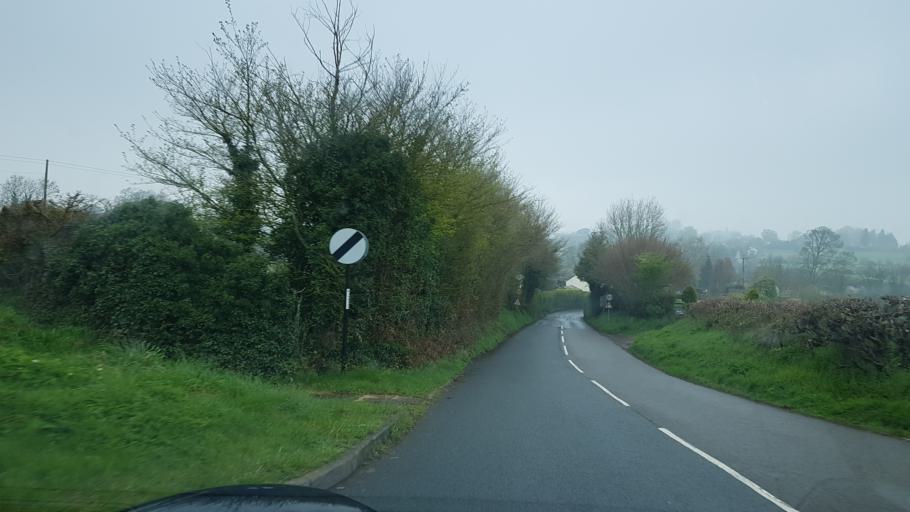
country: GB
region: England
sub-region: Herefordshire
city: Walford
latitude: 51.9179
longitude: -2.6098
